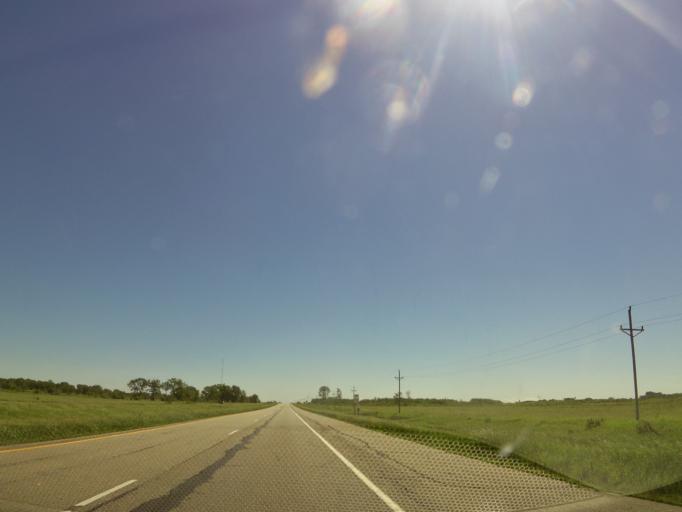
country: US
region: Minnesota
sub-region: Red Lake County
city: Red Lake Falls
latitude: 47.7604
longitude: -96.3601
